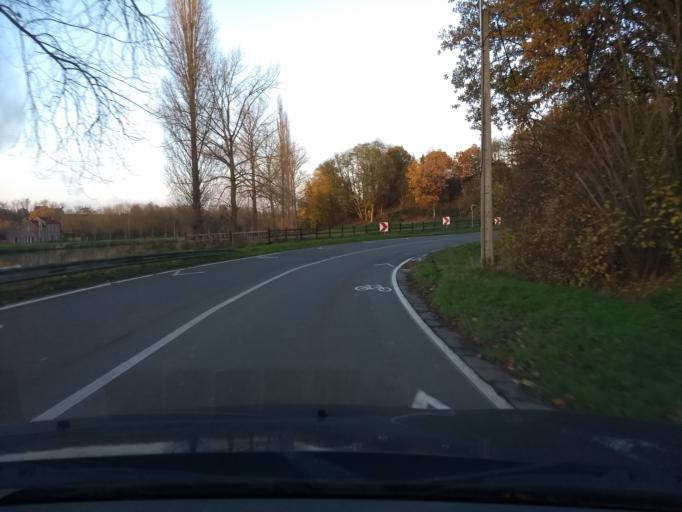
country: BE
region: Wallonia
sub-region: Province du Brabant Wallon
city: Ittre
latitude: 50.6320
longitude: 4.2315
